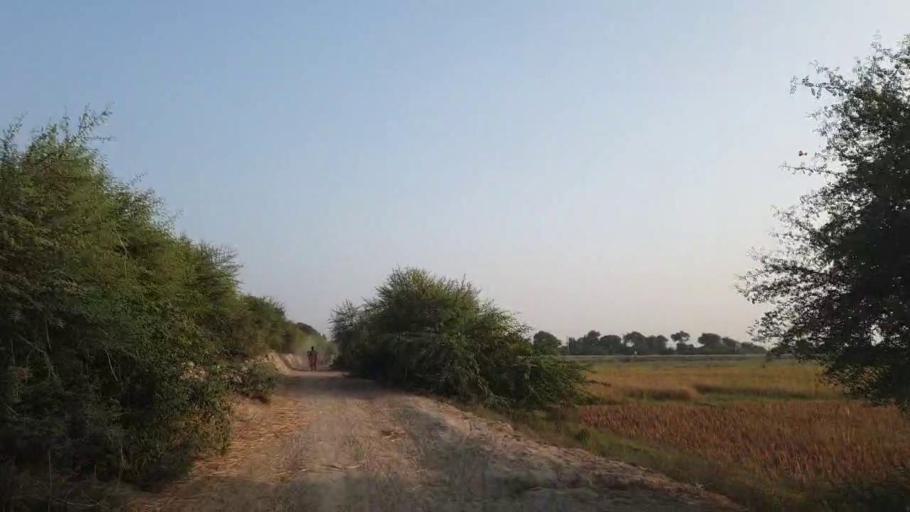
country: PK
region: Sindh
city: Kario
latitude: 24.8500
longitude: 68.6318
